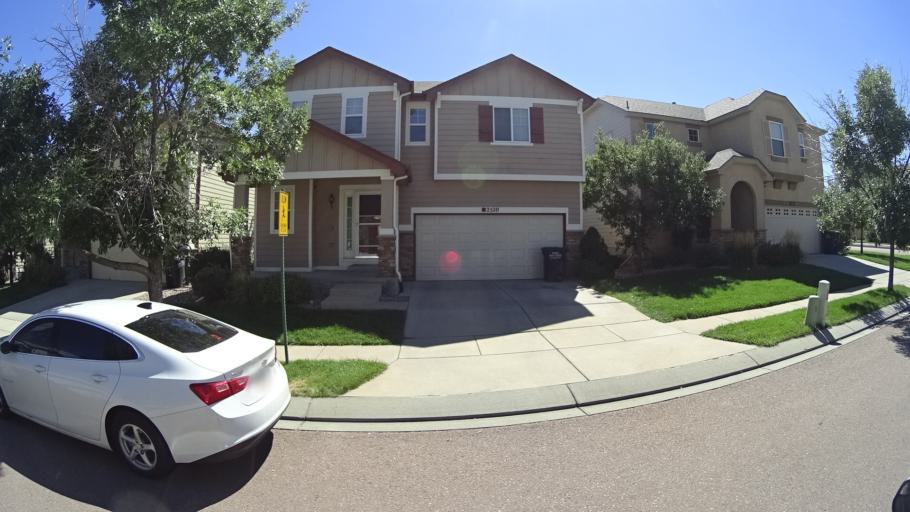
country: US
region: Colorado
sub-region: El Paso County
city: Stratmoor
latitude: 38.7991
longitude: -104.7550
